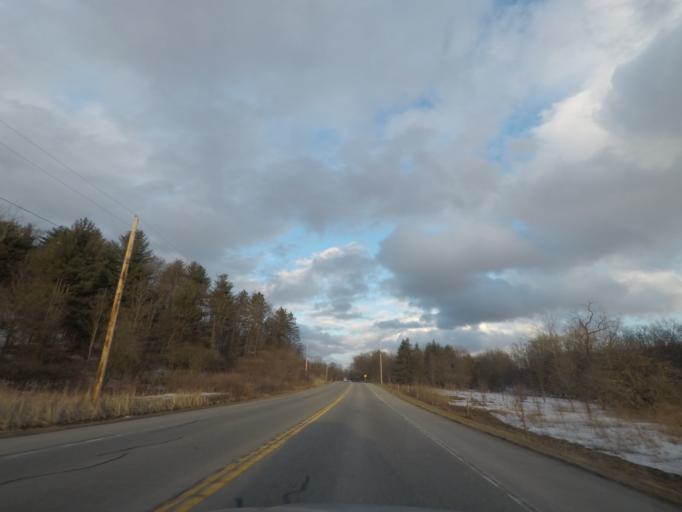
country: US
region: New York
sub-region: Montgomery County
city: Saint Johnsville
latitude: 43.0050
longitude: -74.7316
